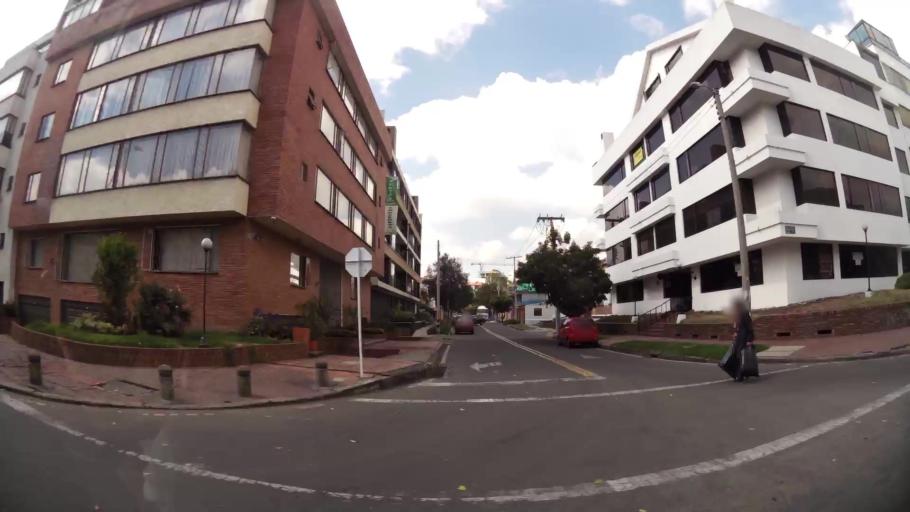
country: CO
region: Bogota D.C.
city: Barrio San Luis
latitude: 4.6961
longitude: -74.0423
